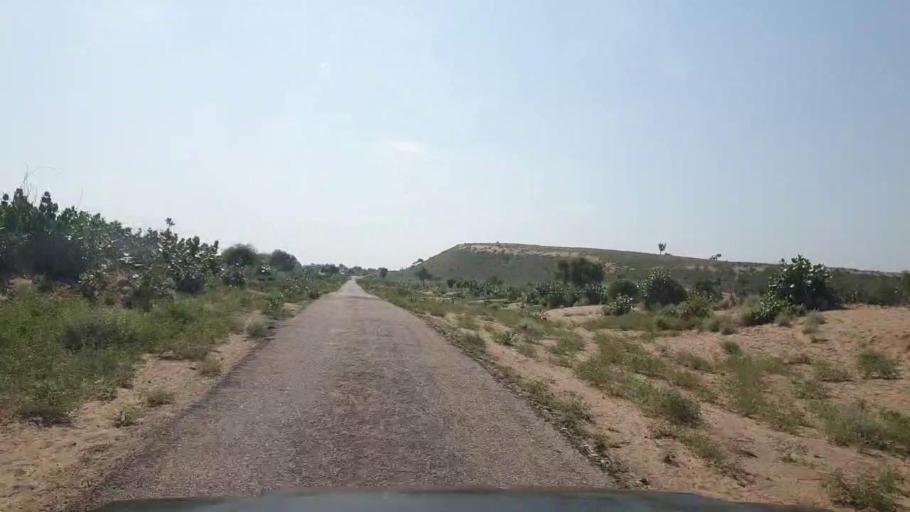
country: PK
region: Sindh
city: Islamkot
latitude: 25.1634
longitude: 70.4051
